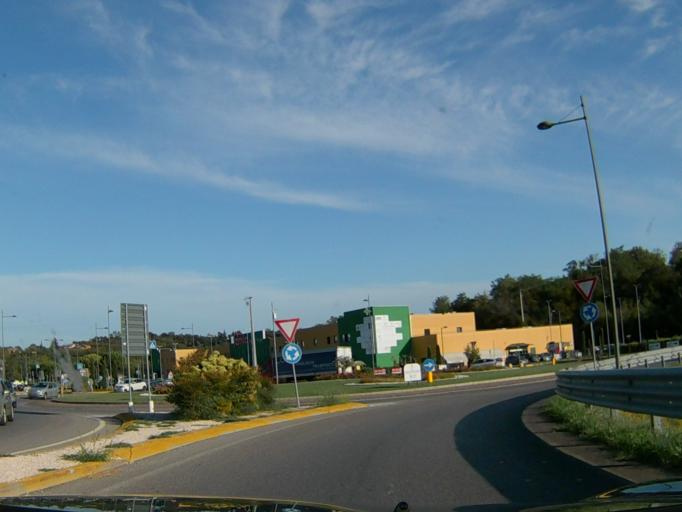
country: IT
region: Lombardy
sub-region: Provincia di Brescia
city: Lonato
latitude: 45.4612
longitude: 10.4902
